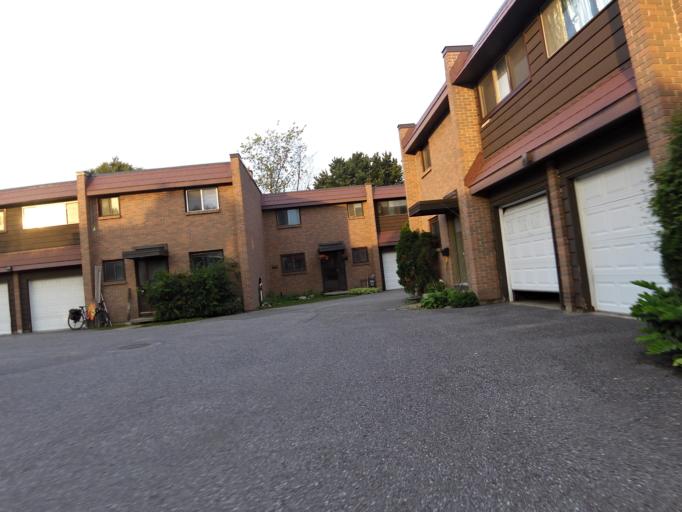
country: CA
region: Ontario
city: Bells Corners
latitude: 45.3159
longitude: -75.8270
